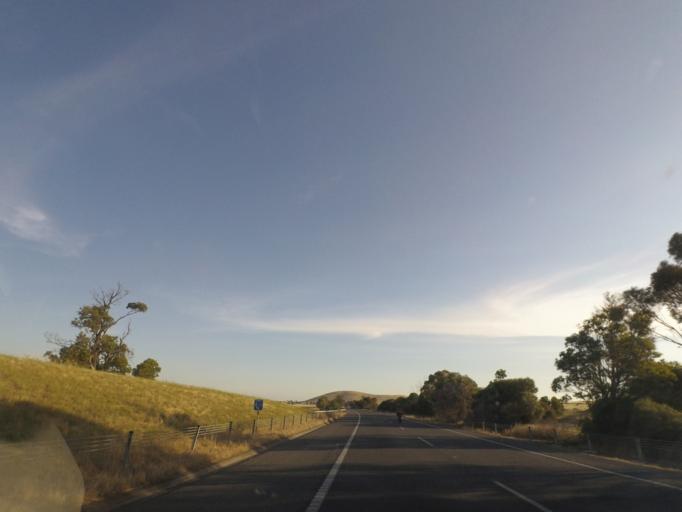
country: AU
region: Victoria
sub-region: Whittlesea
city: Whittlesea
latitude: -37.4376
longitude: 144.9817
